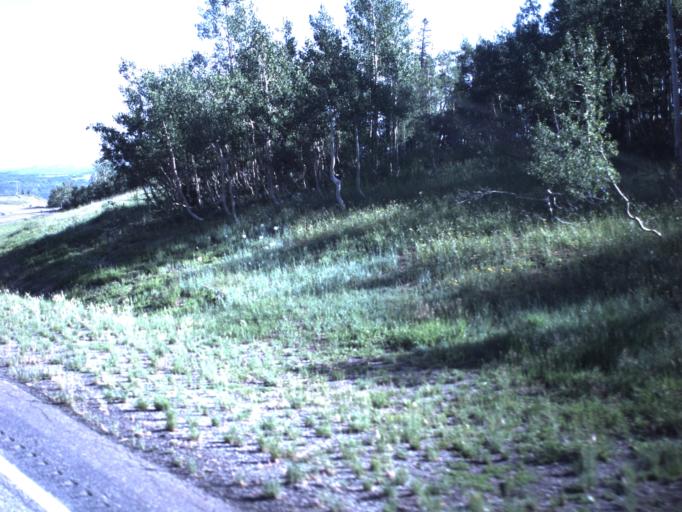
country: US
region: Utah
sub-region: Sanpete County
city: Fairview
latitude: 39.6253
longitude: -111.3211
